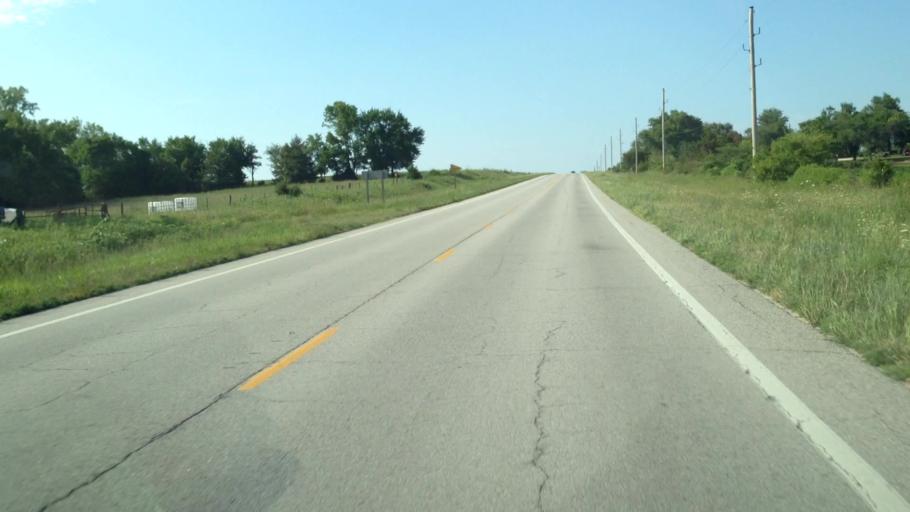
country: US
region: Kansas
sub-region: Allen County
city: Iola
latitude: 37.9963
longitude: -95.1705
